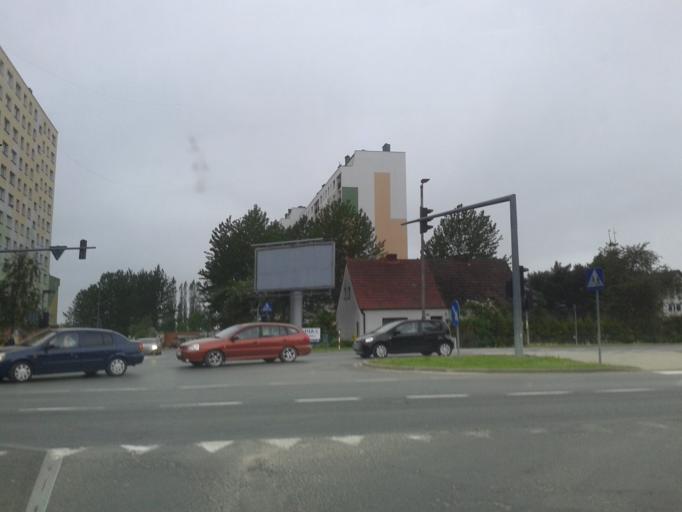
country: PL
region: West Pomeranian Voivodeship
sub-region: Koszalin
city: Koszalin
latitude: 54.2078
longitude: 16.1836
